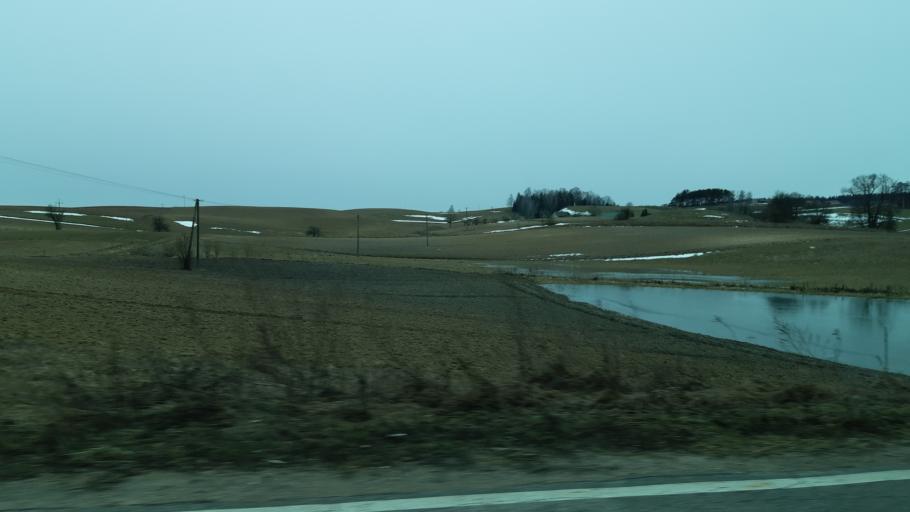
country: PL
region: Podlasie
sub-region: Suwalki
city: Suwalki
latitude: 54.3301
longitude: 22.9546
